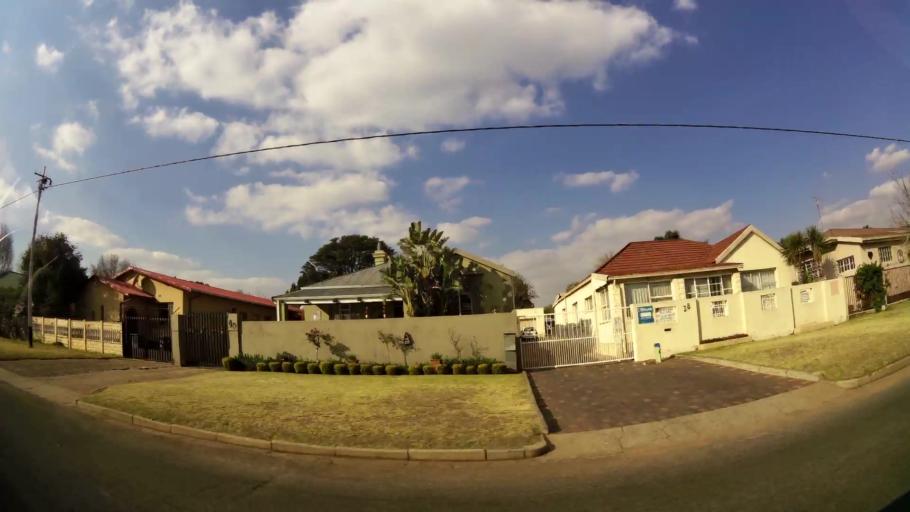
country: ZA
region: Gauteng
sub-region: West Rand District Municipality
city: Krugersdorp
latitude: -26.0891
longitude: 27.7657
